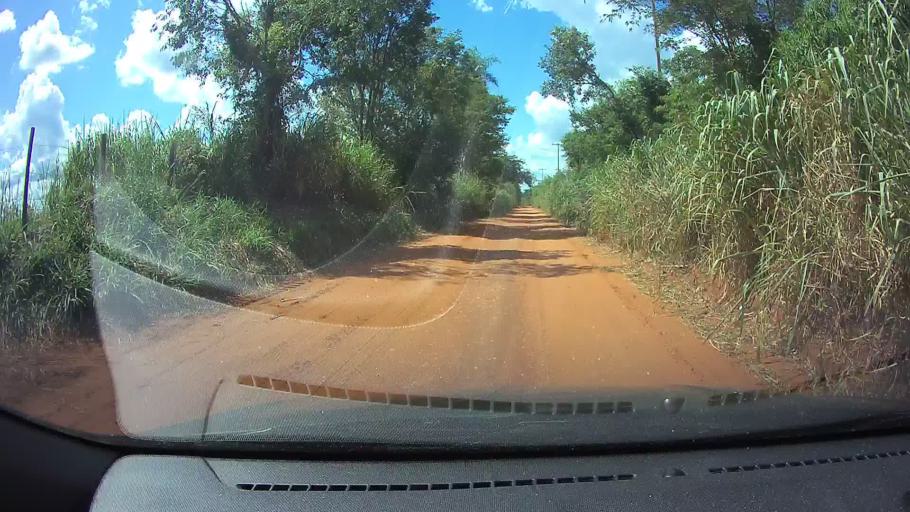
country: PY
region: Paraguari
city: La Colmena
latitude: -25.9083
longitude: -56.7941
